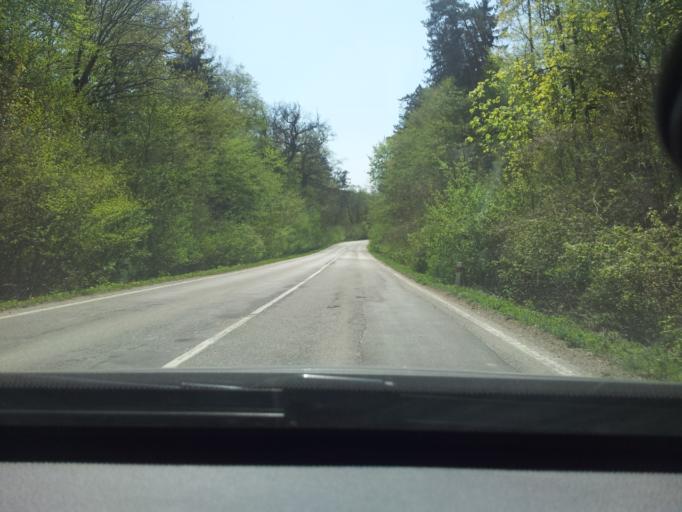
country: SK
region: Nitriansky
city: Zlate Moravce
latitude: 48.4378
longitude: 18.4104
